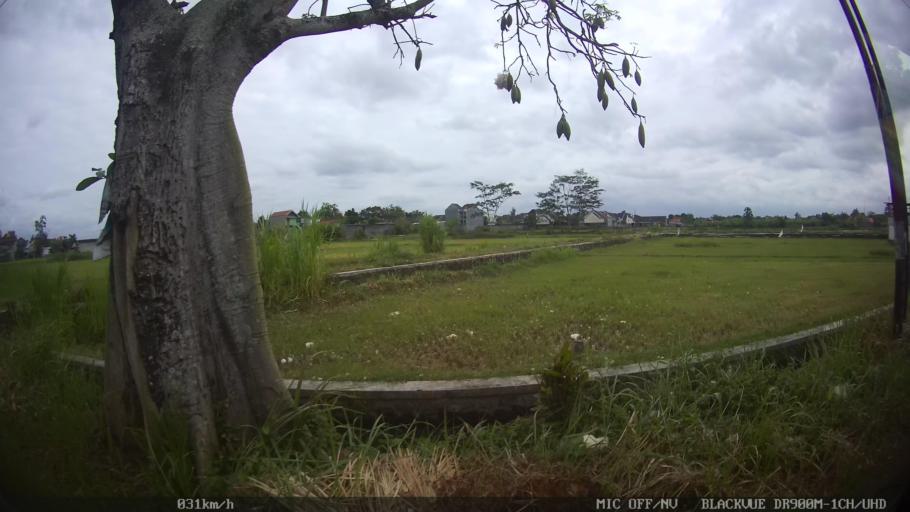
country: ID
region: Daerah Istimewa Yogyakarta
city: Sewon
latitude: -7.8376
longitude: 110.4133
